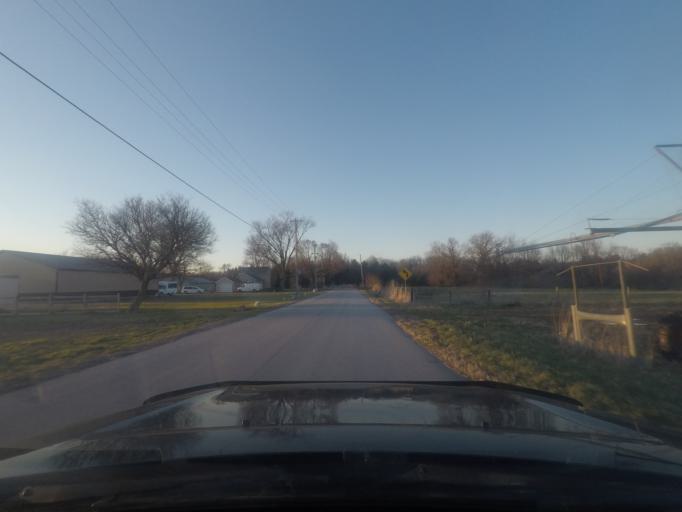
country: US
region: Indiana
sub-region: LaPorte County
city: Kingsford Heights
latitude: 41.5120
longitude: -86.6976
